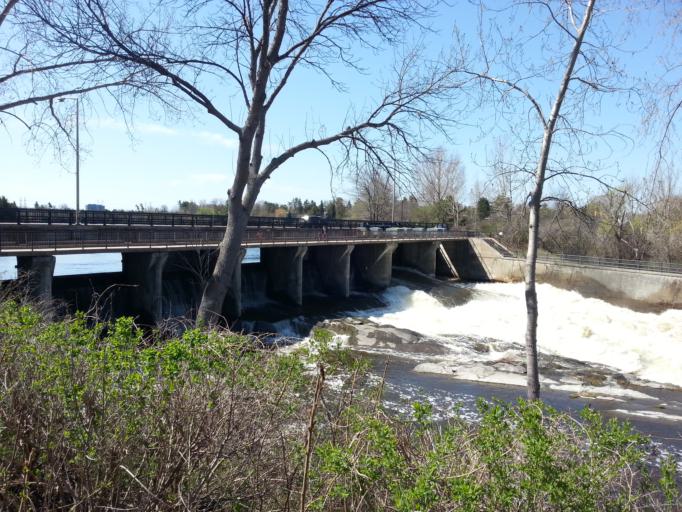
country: CA
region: Ontario
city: Ottawa
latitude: 45.3714
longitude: -75.6963
